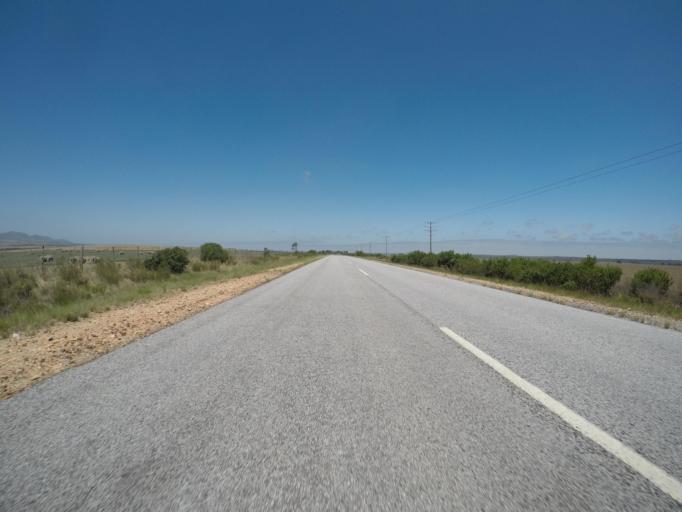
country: ZA
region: Eastern Cape
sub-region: Cacadu District Municipality
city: Kruisfontein
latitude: -34.0137
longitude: 24.5653
